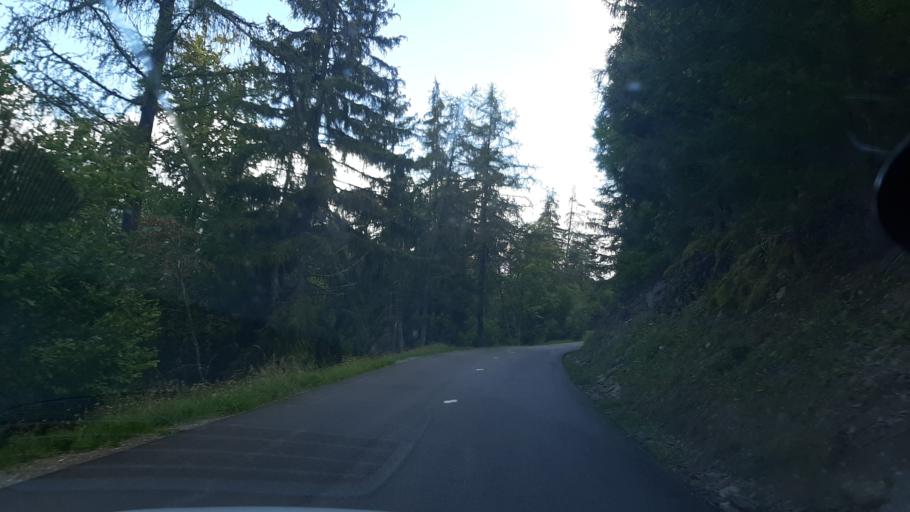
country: FR
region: Rhone-Alpes
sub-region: Departement de la Savoie
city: Aime
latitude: 45.5220
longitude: 6.6026
